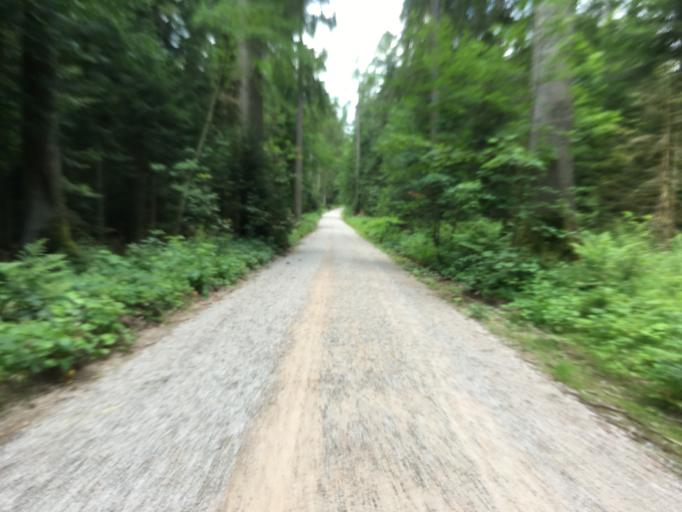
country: DE
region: Baden-Wuerttemberg
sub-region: Karlsruhe Region
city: Freudenstadt
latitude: 48.4508
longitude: 8.4094
